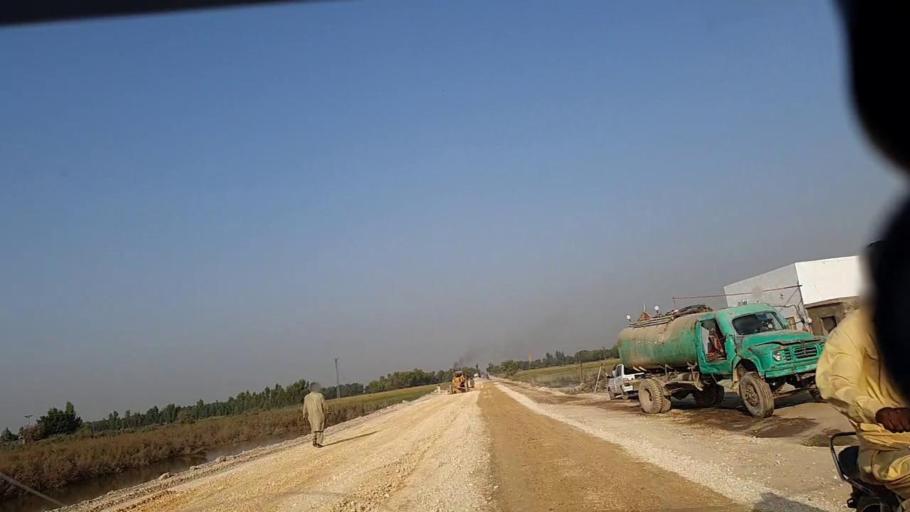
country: PK
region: Sindh
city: Chak
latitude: 27.8502
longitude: 68.8096
